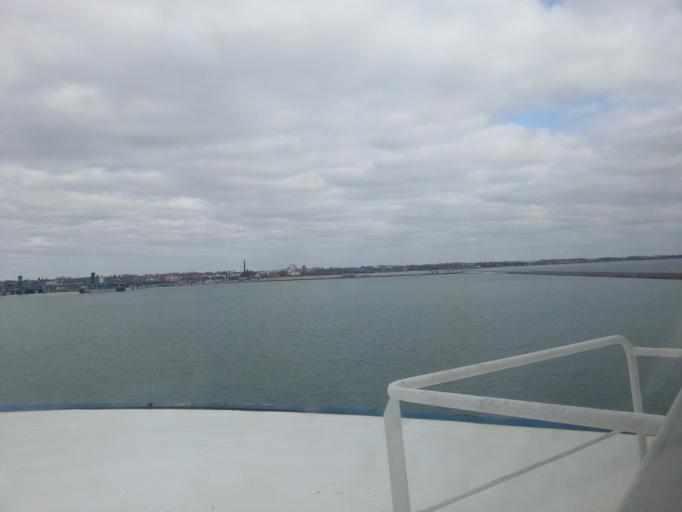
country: SE
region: Skane
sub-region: Trelleborgs Kommun
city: Trelleborg
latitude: 55.3599
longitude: 13.1489
